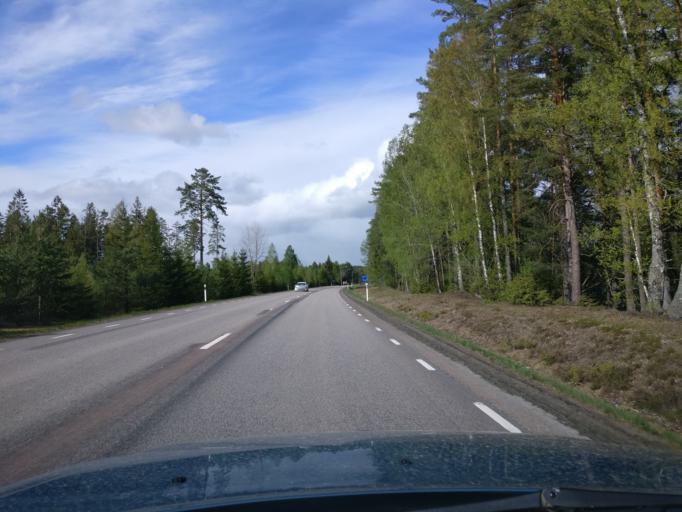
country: SE
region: Vaermland
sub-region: Forshaga Kommun
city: Forshaga
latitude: 59.5079
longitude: 13.4368
